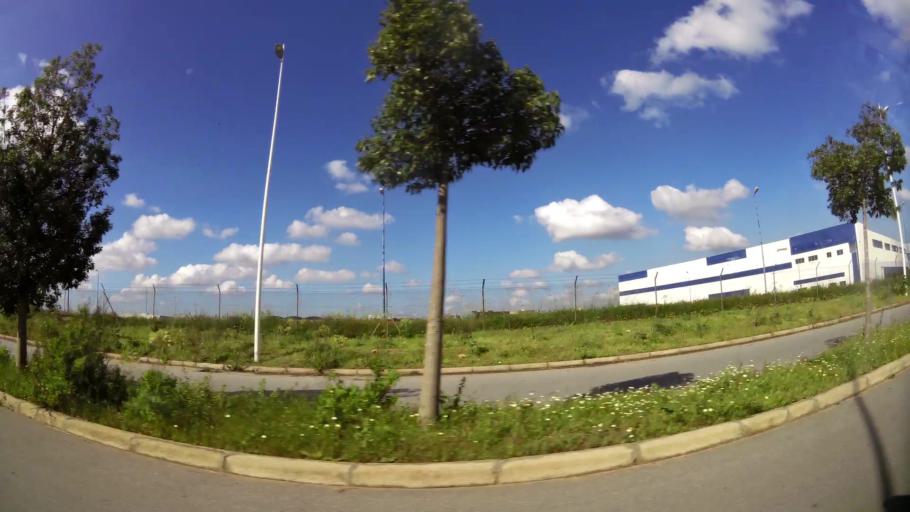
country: MA
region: Grand Casablanca
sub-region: Mediouna
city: Mediouna
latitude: 33.3896
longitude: -7.5410
